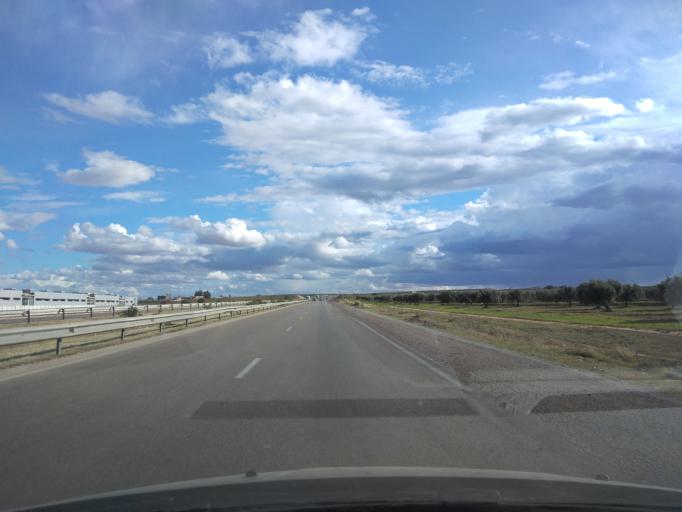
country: TN
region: Al Munastir
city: Manzil Kamil
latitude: 35.5621
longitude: 10.6156
